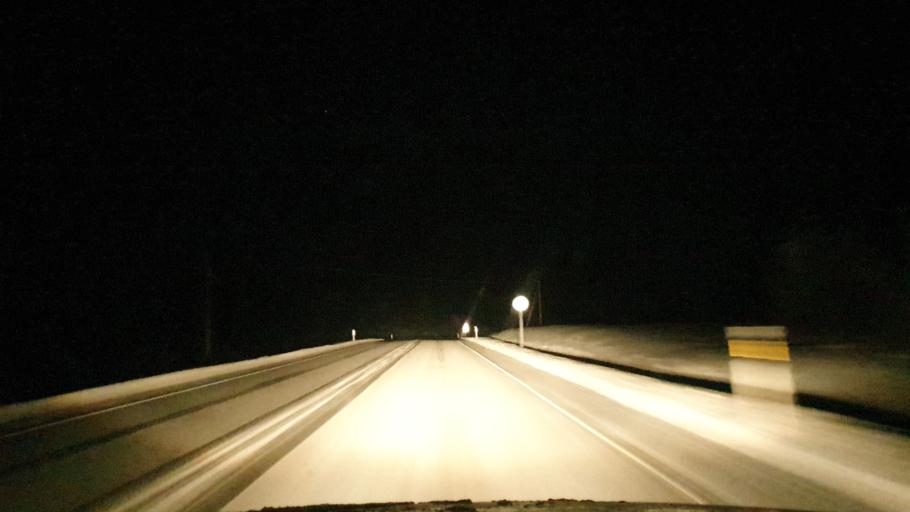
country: EE
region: Jogevamaa
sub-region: Jogeva linn
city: Jogeva
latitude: 58.6918
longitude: 26.4554
